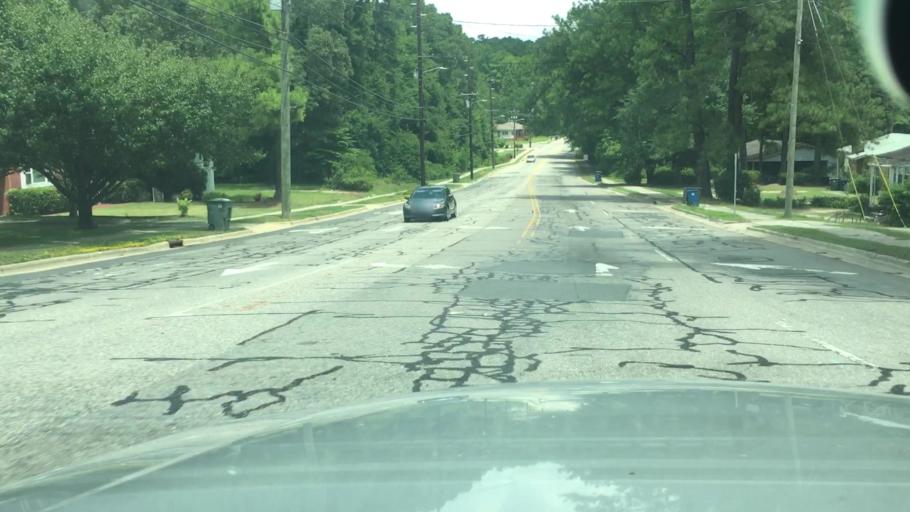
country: US
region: North Carolina
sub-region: Cumberland County
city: Fayetteville
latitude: 35.0792
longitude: -78.8900
